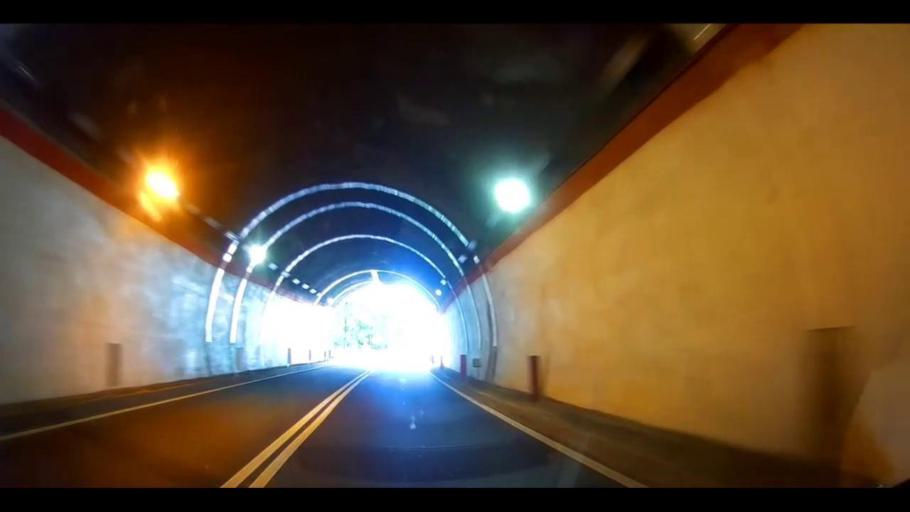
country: IT
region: Calabria
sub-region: Provincia di Cosenza
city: Celico
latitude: 39.3045
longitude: 16.3543
